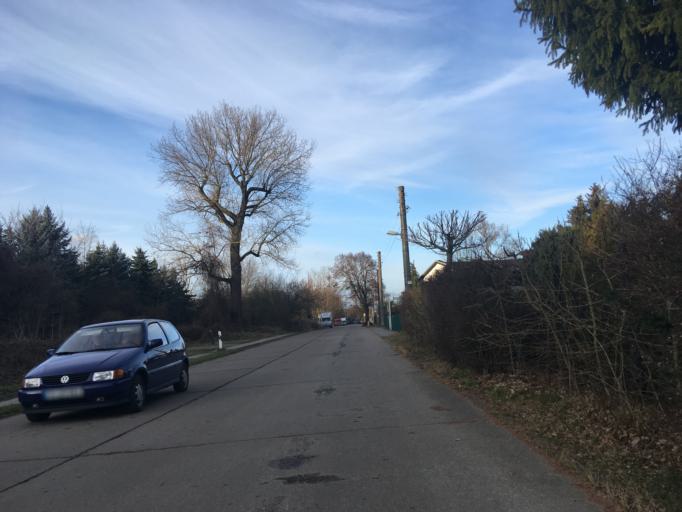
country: DE
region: Berlin
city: Blankenfelde
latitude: 52.6391
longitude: 13.4006
